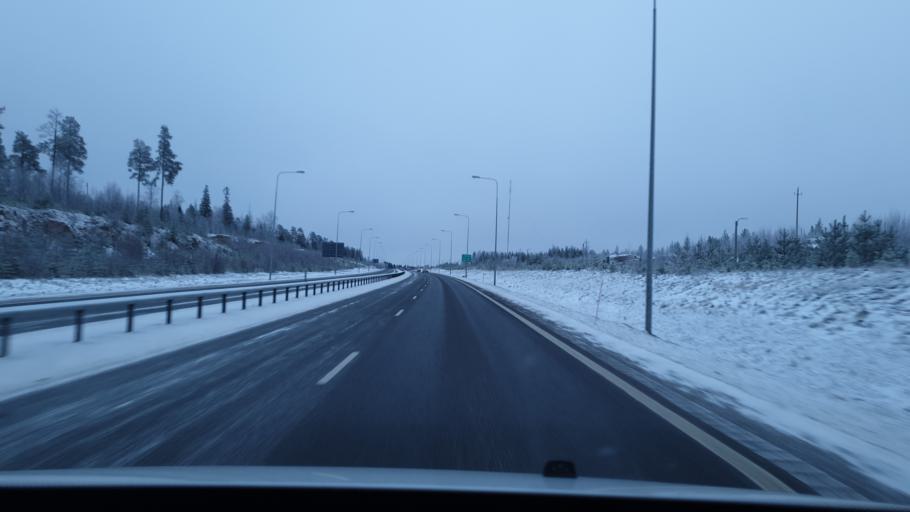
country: FI
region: Lapland
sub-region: Kemi-Tornio
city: Kemi
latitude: 65.6910
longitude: 24.6906
